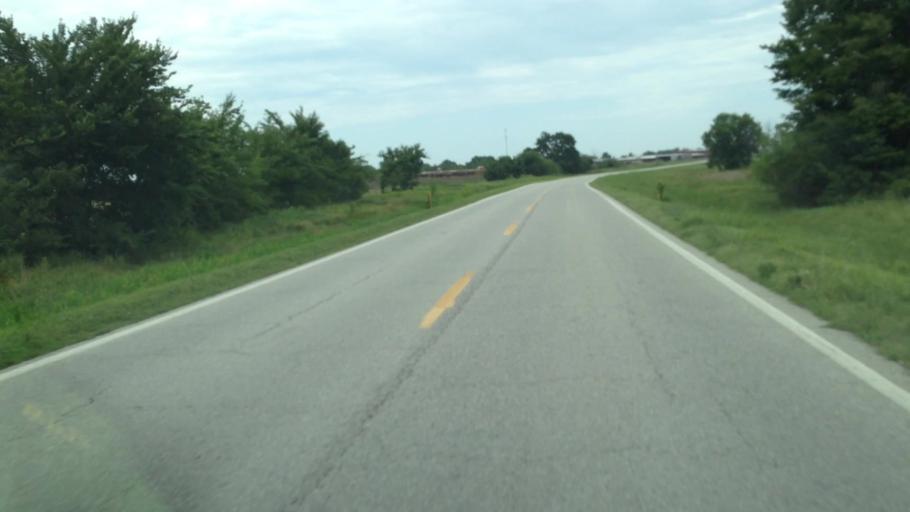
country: US
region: Kansas
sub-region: Labette County
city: Chetopa
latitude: 36.8604
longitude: -95.1134
